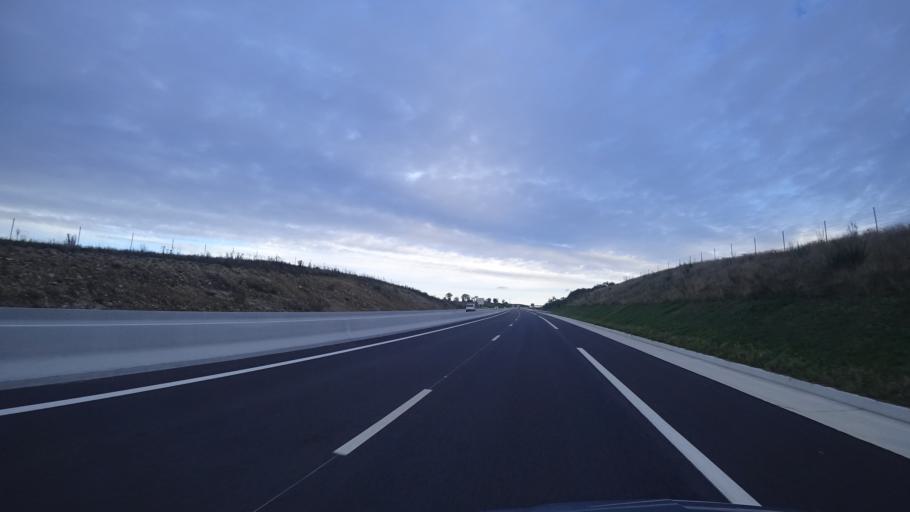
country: FR
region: Midi-Pyrenees
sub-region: Departement de l'Aveyron
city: Baraqueville
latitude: 44.2901
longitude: 2.4589
